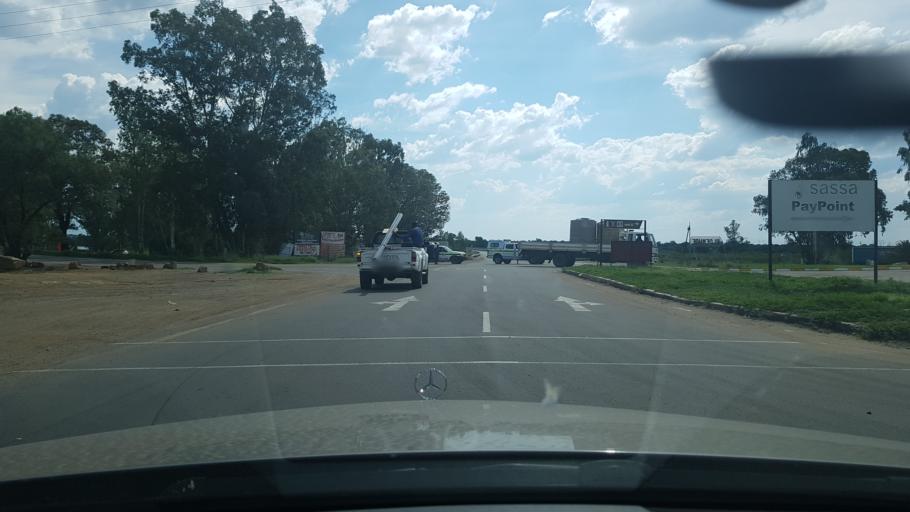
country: ZA
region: North-West
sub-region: Dr Ruth Segomotsi Mompati District Municipality
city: Bloemhof
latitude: -27.6525
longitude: 25.5966
